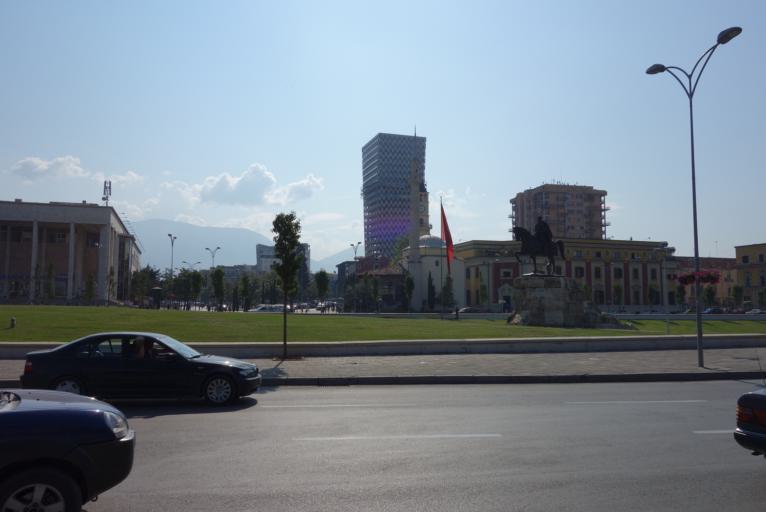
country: AL
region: Tirane
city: Tirana
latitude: 41.3280
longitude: 19.8179
